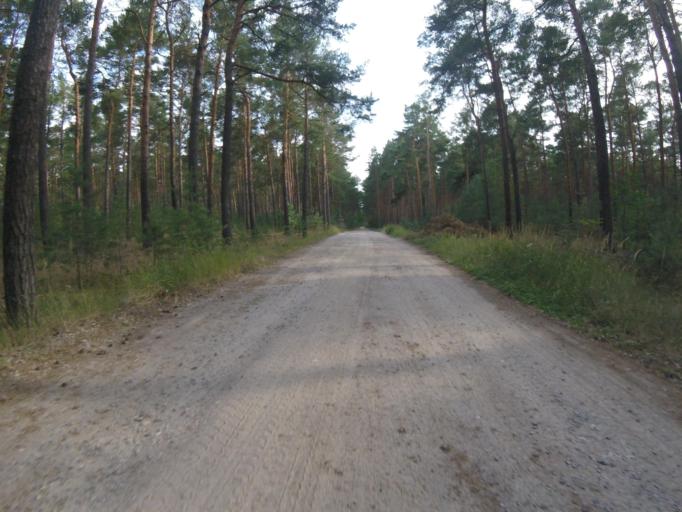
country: DE
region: Brandenburg
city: Bestensee
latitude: 52.2308
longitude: 13.7581
